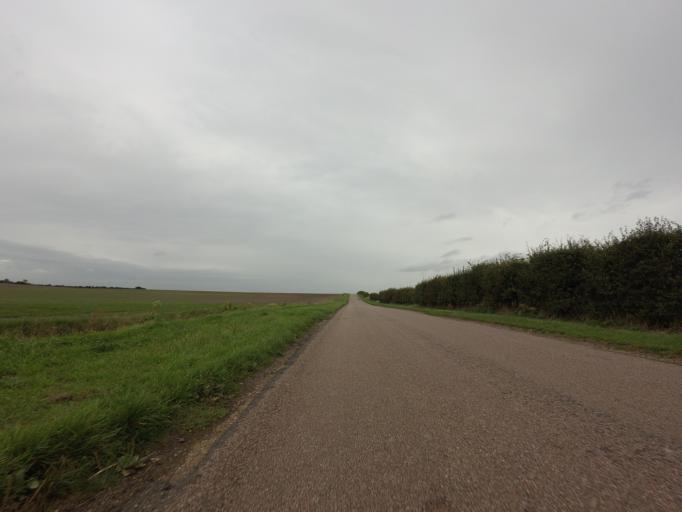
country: GB
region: England
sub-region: Cambridgeshire
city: Harston
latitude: 52.0719
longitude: 0.0916
